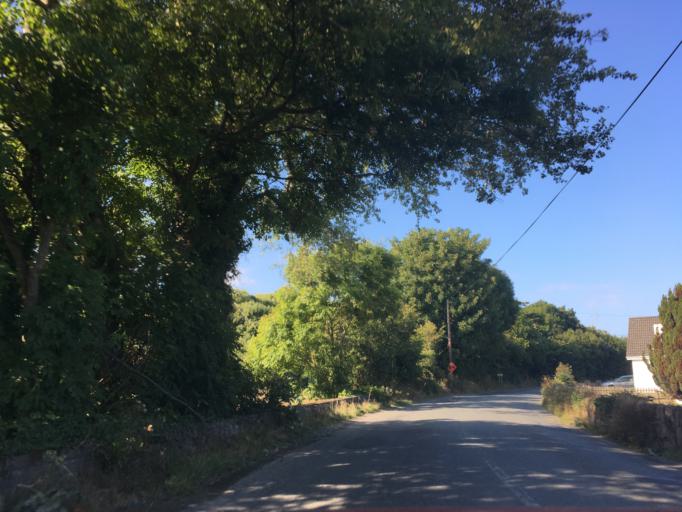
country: IE
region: Leinster
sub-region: Loch Garman
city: Loch Garman
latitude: 52.2641
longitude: -6.4820
